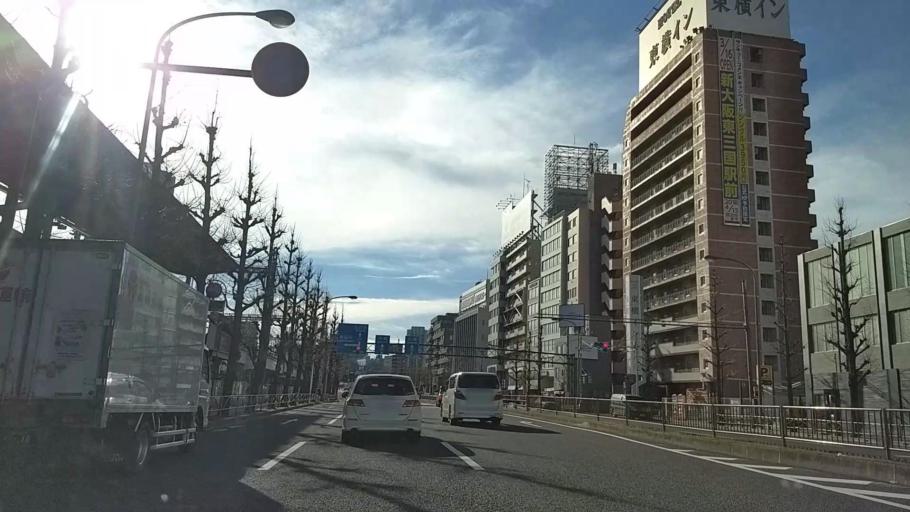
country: JP
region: Tokyo
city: Tokyo
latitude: 35.6273
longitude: 139.7377
